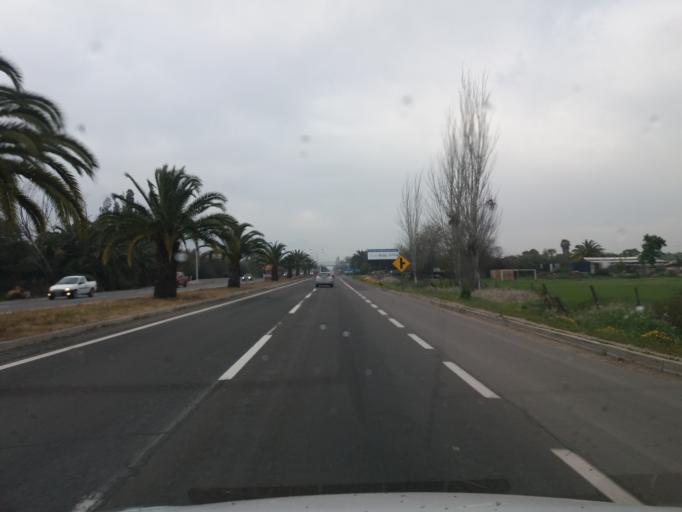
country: CL
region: Valparaiso
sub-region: Provincia de Quillota
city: Hacienda La Calera
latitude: -32.7759
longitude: -71.1834
